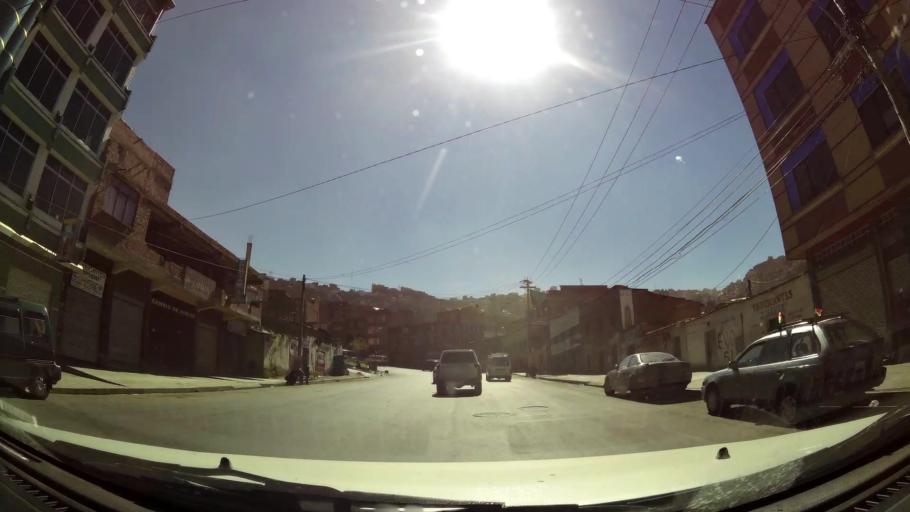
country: BO
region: La Paz
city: La Paz
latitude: -16.4916
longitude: -68.1641
